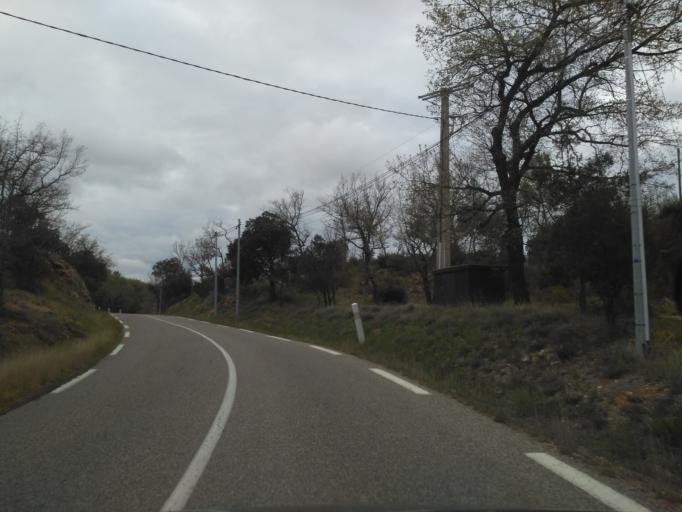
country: FR
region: Provence-Alpes-Cote d'Azur
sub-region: Departement du Var
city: Barjols
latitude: 43.6138
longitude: 5.9497
